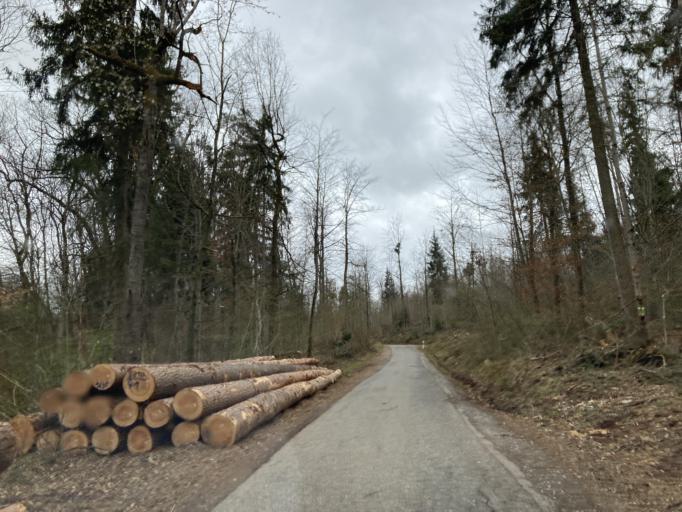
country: DE
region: Baden-Wuerttemberg
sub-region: Tuebingen Region
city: Tuebingen
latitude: 48.4914
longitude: 9.0790
